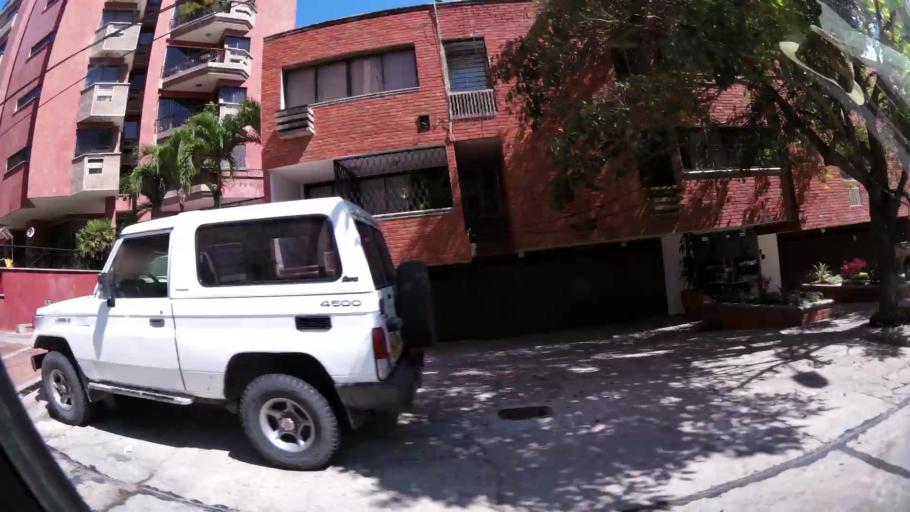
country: CO
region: Atlantico
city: Barranquilla
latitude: 11.0088
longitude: -74.8120
